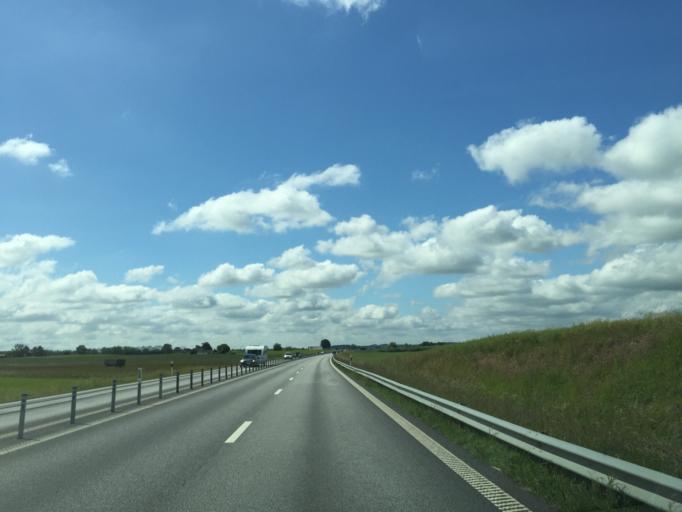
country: SE
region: Skane
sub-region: Skurups Kommun
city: Rydsgard
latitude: 55.4834
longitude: 13.5852
